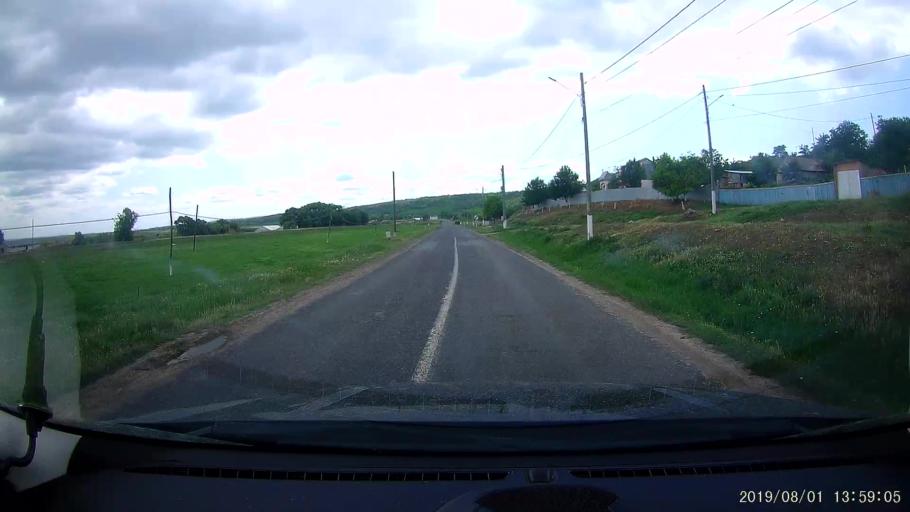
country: RO
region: Galati
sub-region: Comuna Foltesti
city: Foltesti
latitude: 45.7801
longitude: 28.0771
